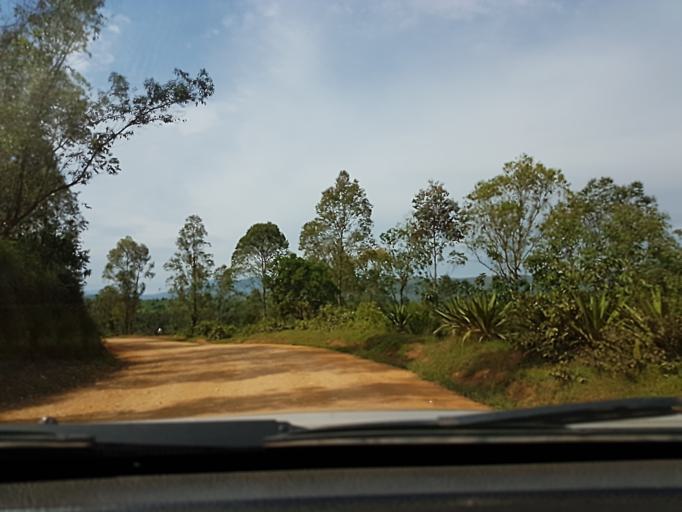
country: CD
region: South Kivu
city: Bukavu
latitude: -2.6250
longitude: 28.8746
